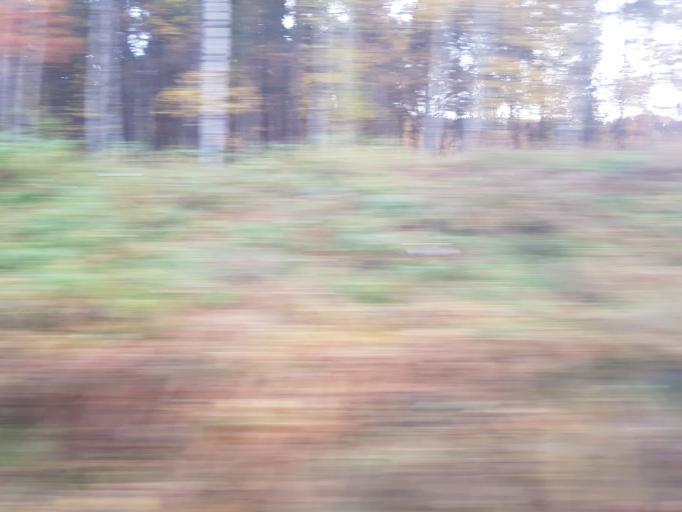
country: NO
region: Oppland
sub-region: Dovre
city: Dovre
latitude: 61.9705
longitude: 9.2562
